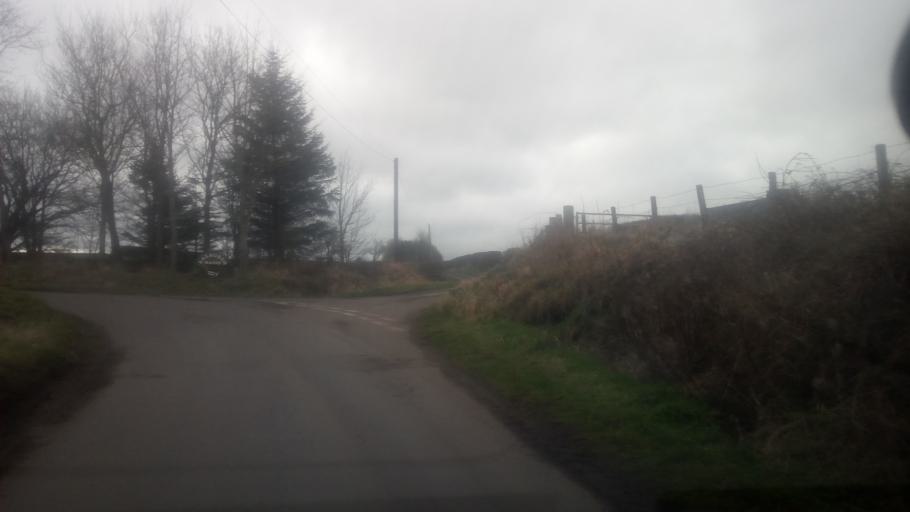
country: GB
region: Scotland
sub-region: The Scottish Borders
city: Kelso
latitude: 55.5660
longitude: -2.4829
